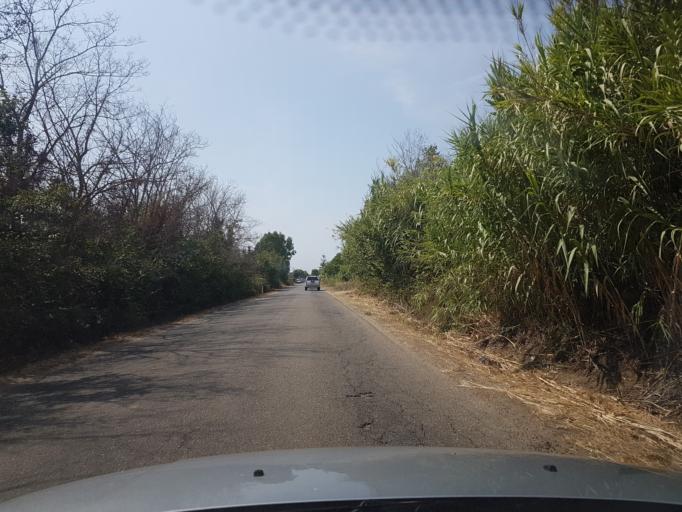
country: IT
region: Sardinia
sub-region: Provincia di Oristano
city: Solanas
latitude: 39.9218
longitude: 8.5444
